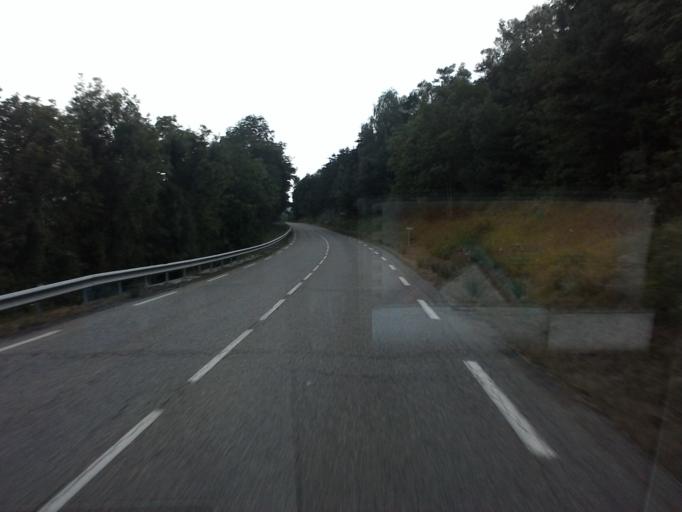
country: FR
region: Provence-Alpes-Cote d'Azur
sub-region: Departement des Hautes-Alpes
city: Saint-Bonnet-en-Champsaur
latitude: 44.7397
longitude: 6.0066
